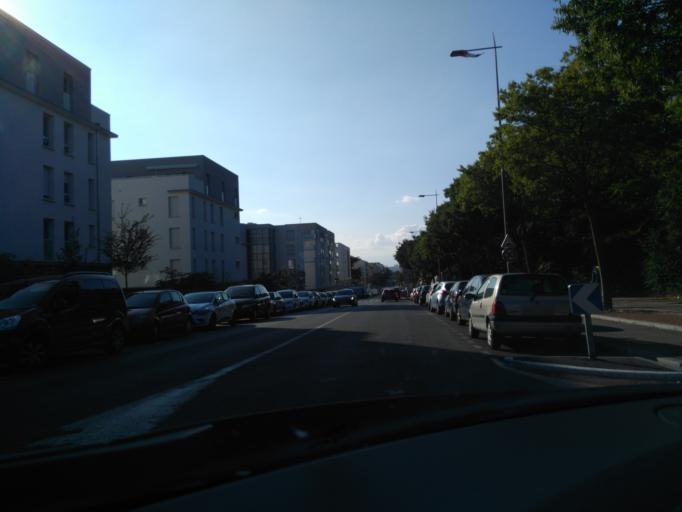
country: FR
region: Rhone-Alpes
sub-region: Departement du Rhone
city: Bron
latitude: 45.7297
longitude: 4.9201
